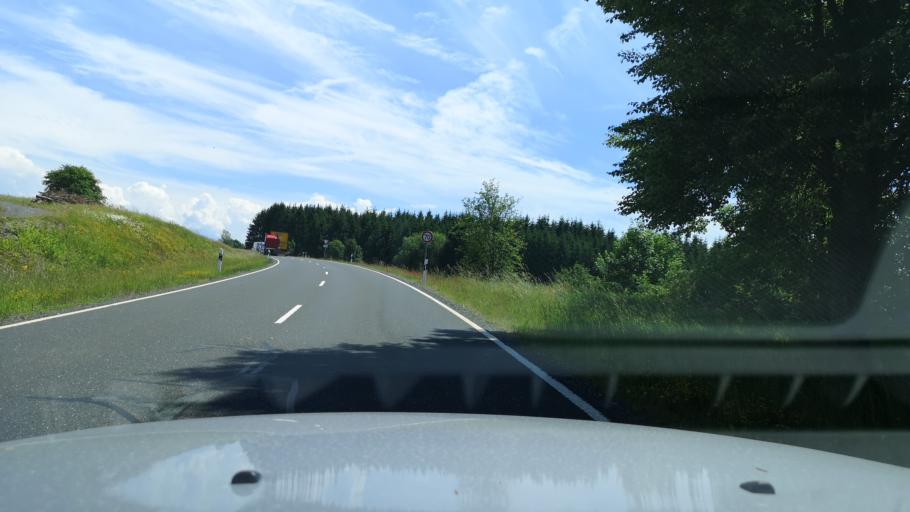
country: DE
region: Bavaria
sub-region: Upper Franconia
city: Nordhalben
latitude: 50.3838
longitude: 11.5001
